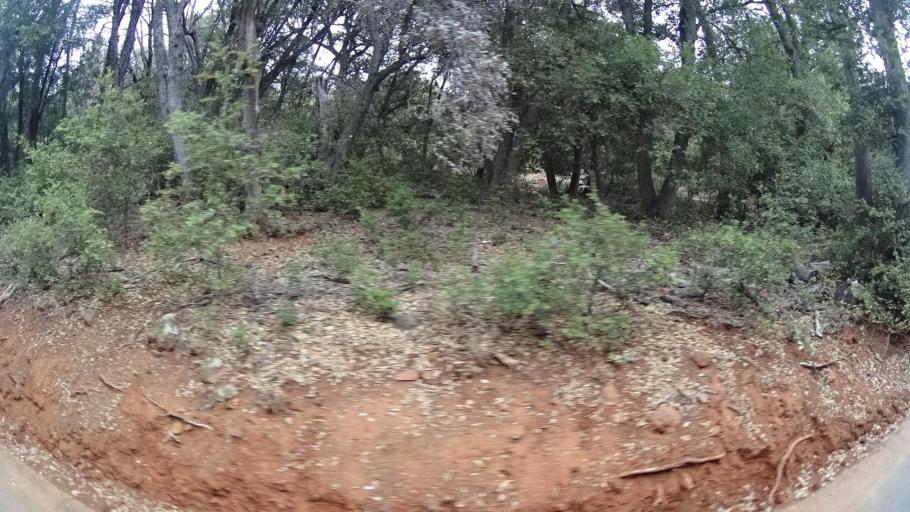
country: US
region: California
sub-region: San Diego County
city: Julian
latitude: 33.0435
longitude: -116.6300
